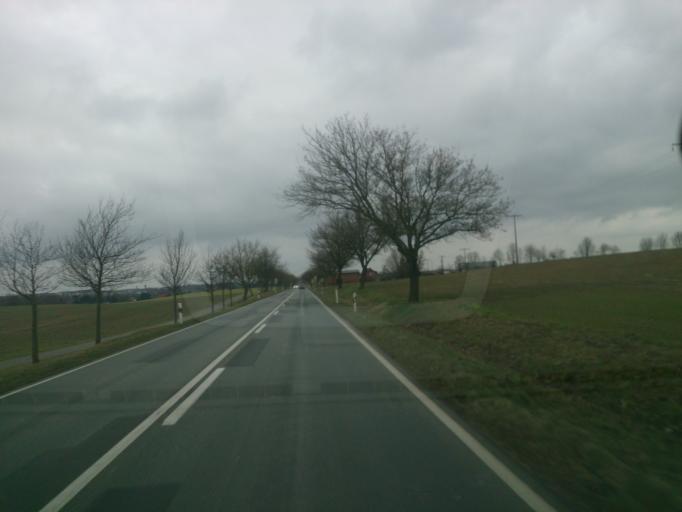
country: DE
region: Mecklenburg-Vorpommern
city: Wackerow
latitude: 53.6768
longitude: 12.9069
